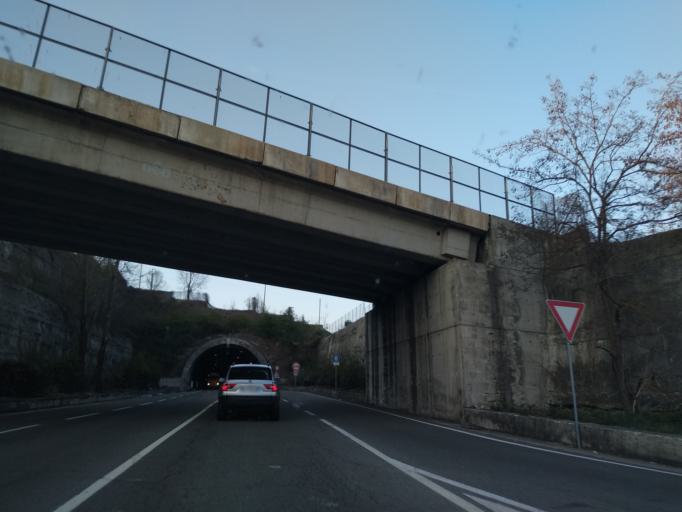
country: IT
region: Emilia-Romagna
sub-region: Provincia di Reggio Emilia
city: Carpineti
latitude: 44.4721
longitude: 10.4905
